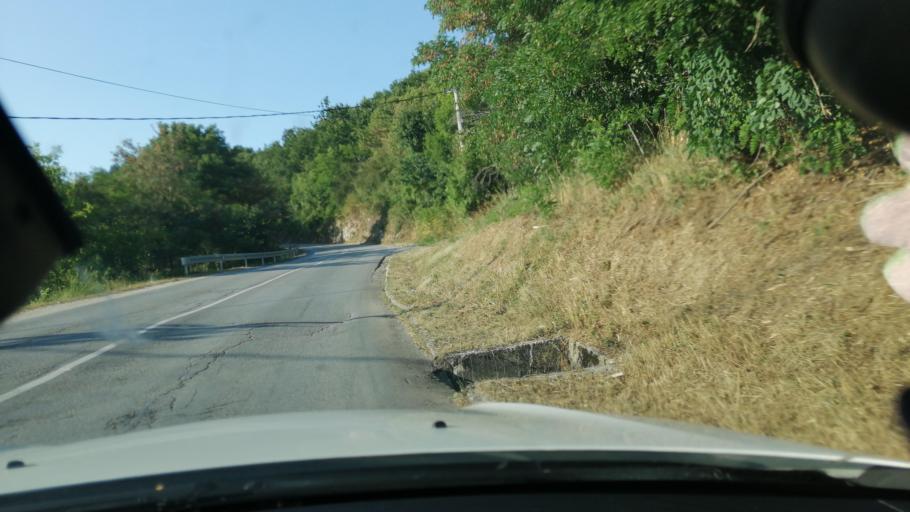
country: RS
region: Central Serbia
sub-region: Moravicki Okrug
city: Ivanjica
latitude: 43.6376
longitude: 20.2407
